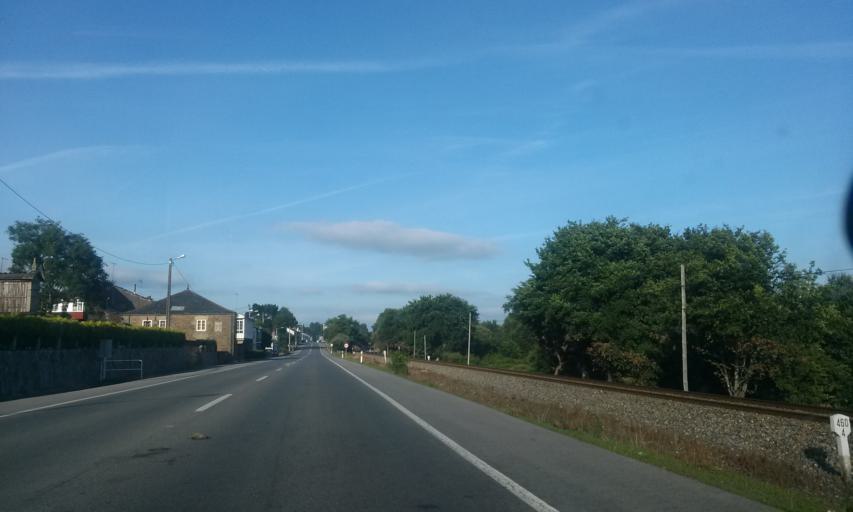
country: ES
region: Galicia
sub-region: Provincia de Lugo
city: Begonte
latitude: 43.1729
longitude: -7.7640
